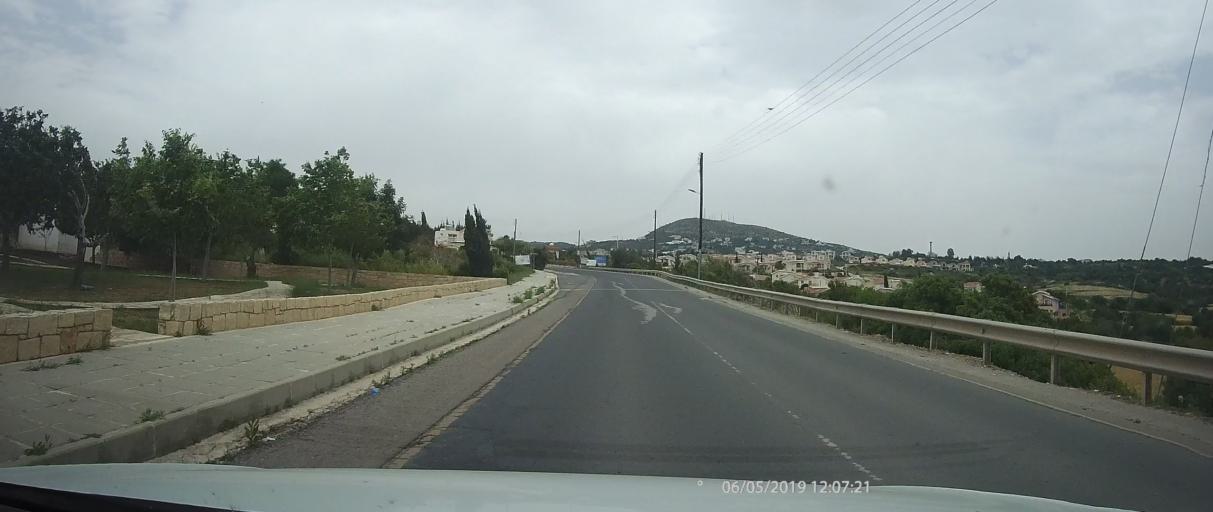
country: CY
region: Pafos
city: Tala
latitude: 34.8270
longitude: 32.4275
